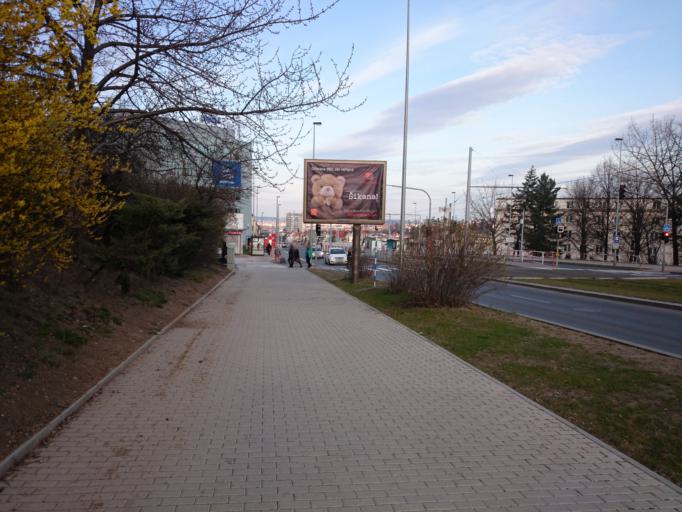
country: CZ
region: Central Bohemia
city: Horomerice
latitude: 50.0987
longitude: 14.3629
